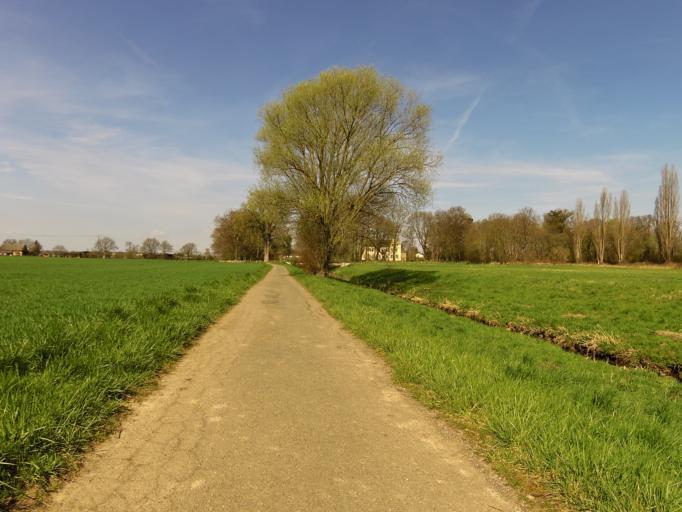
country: DE
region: North Rhine-Westphalia
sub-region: Regierungsbezirk Koln
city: Rheinbach
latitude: 50.6624
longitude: 6.9615
